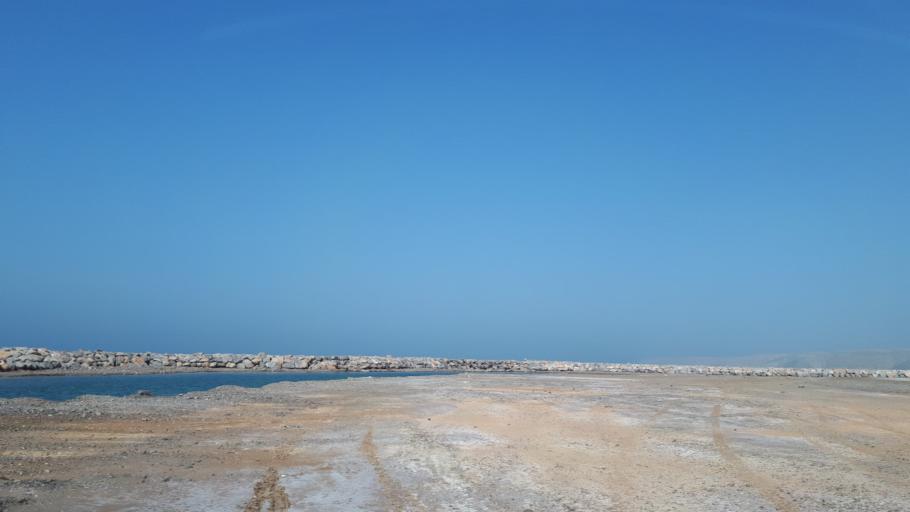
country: OM
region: Muhafazat Masqat
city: Muscat
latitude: 23.5461
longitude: 58.6688
